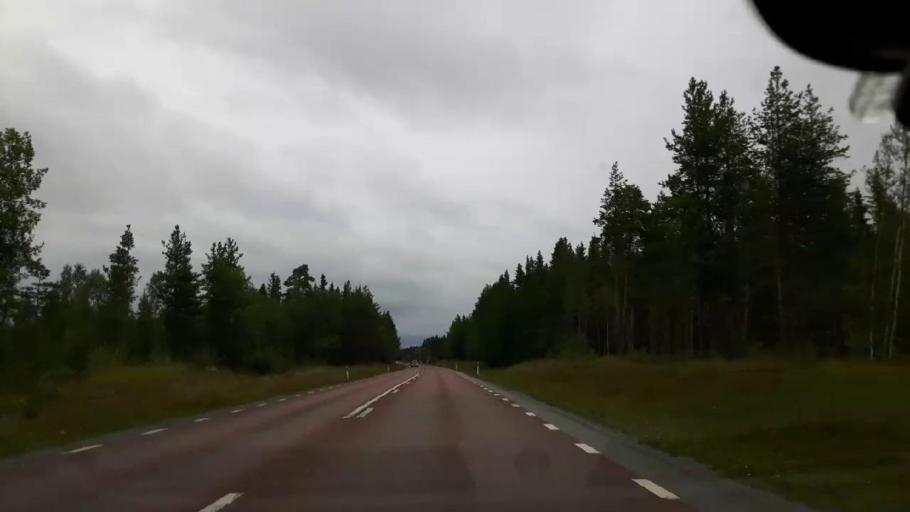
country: SE
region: Jaemtland
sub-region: Bergs Kommun
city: Hoverberg
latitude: 62.9217
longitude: 14.5330
